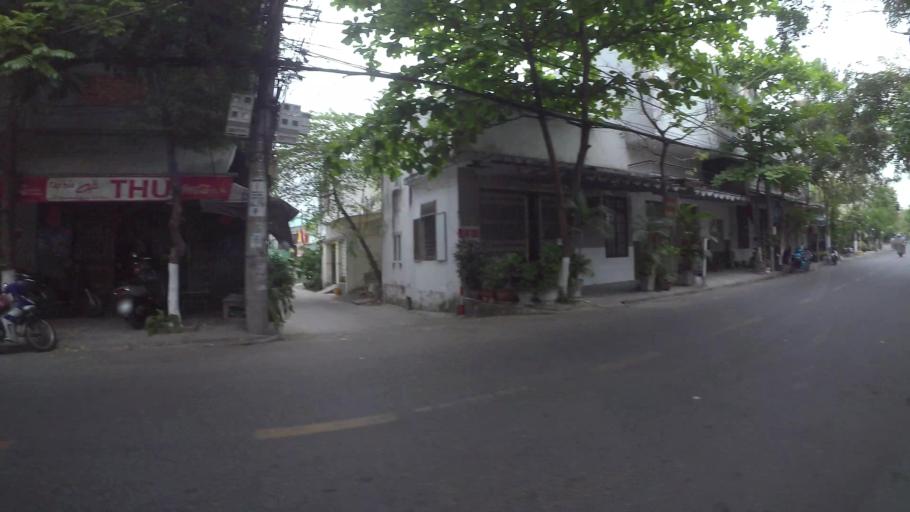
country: VN
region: Da Nang
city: Thanh Khe
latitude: 16.0493
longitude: 108.1858
